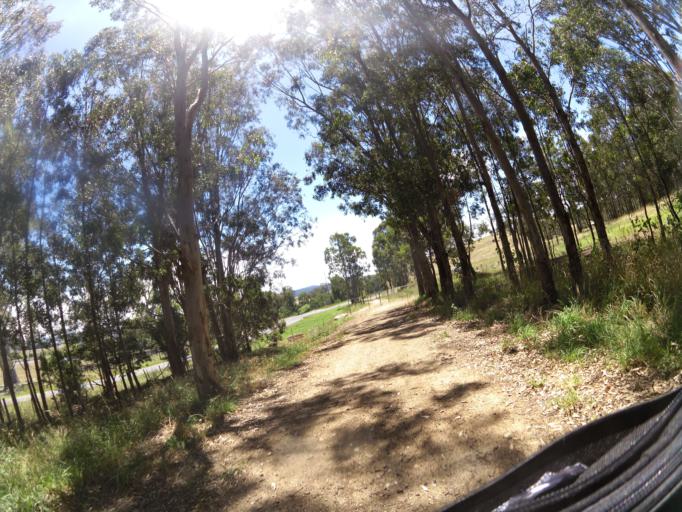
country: AU
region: Victoria
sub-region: East Gippsland
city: Lakes Entrance
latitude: -37.7225
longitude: 147.8483
